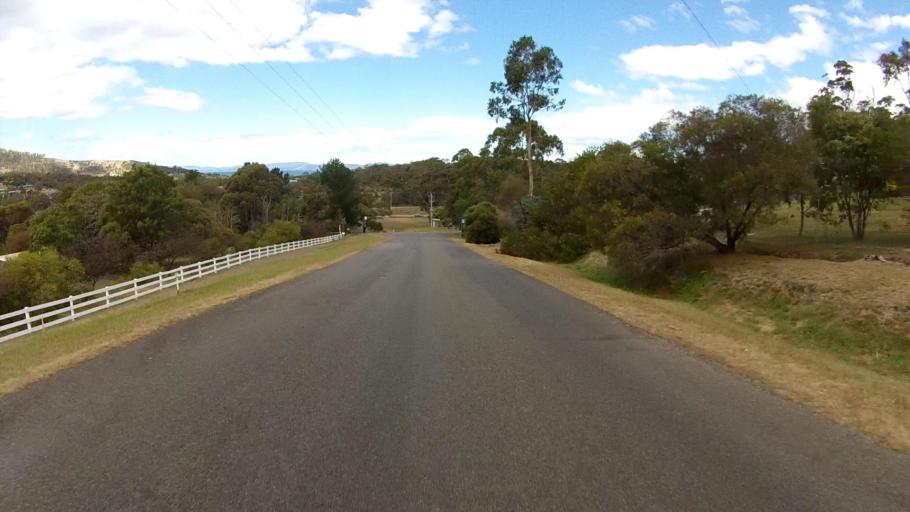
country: AU
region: Tasmania
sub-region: Clarence
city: Acton Park
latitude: -42.8703
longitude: 147.4715
